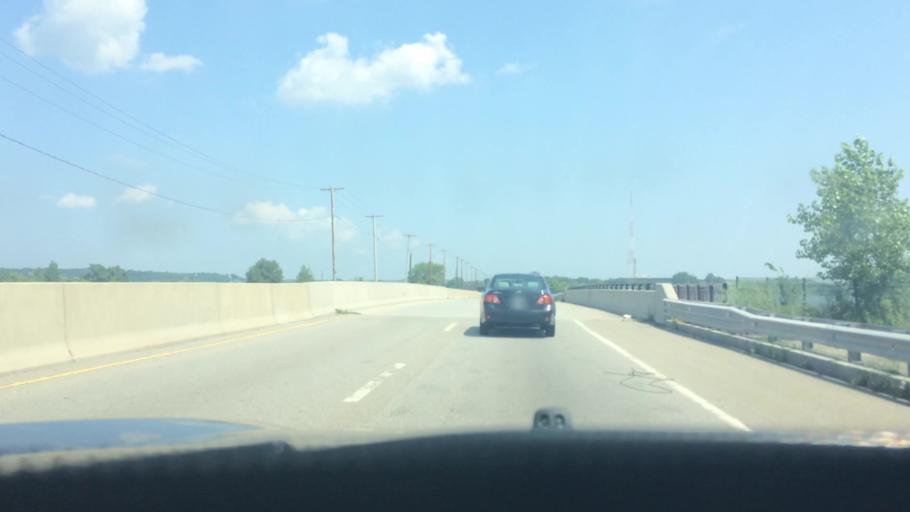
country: US
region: Massachusetts
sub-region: Suffolk County
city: Revere
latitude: 42.4305
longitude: -70.9977
